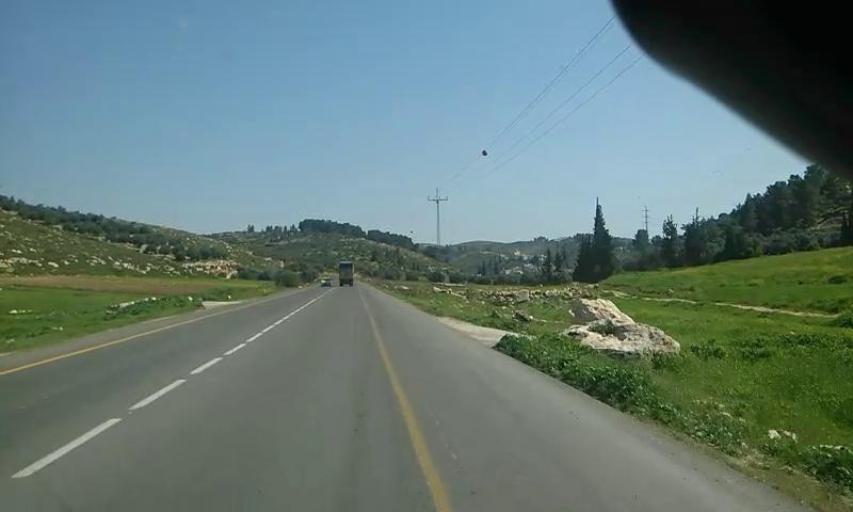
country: PS
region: West Bank
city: Idhna
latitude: 31.5758
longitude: 34.9807
